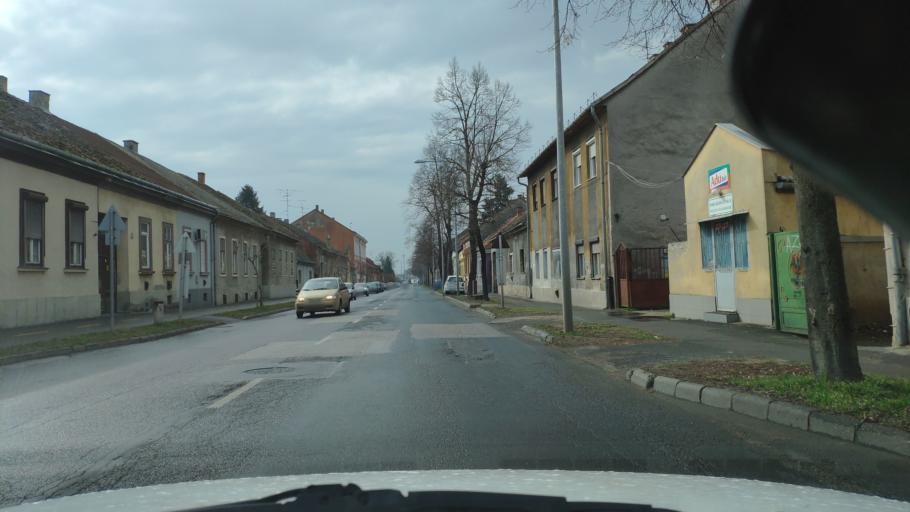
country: HU
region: Zala
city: Nagykanizsa
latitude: 46.4473
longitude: 16.9910
